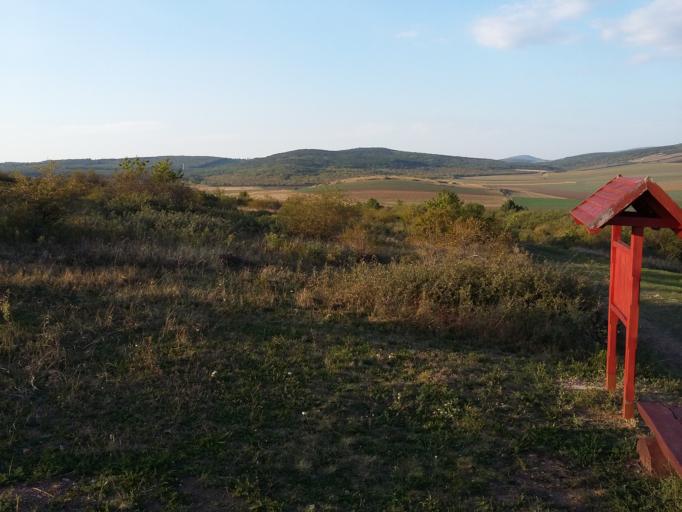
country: HU
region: Borsod-Abauj-Zemplen
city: Bekecs
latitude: 48.1583
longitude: 21.1729
